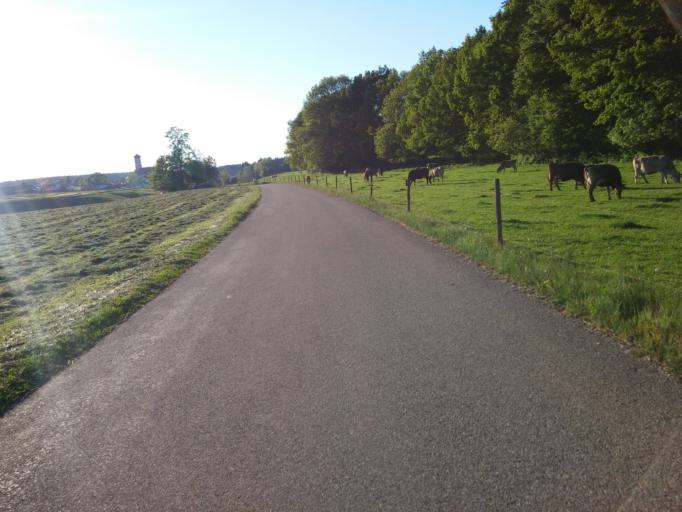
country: DE
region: Bavaria
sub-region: Swabia
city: Kronburg
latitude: 47.8844
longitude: 10.1476
